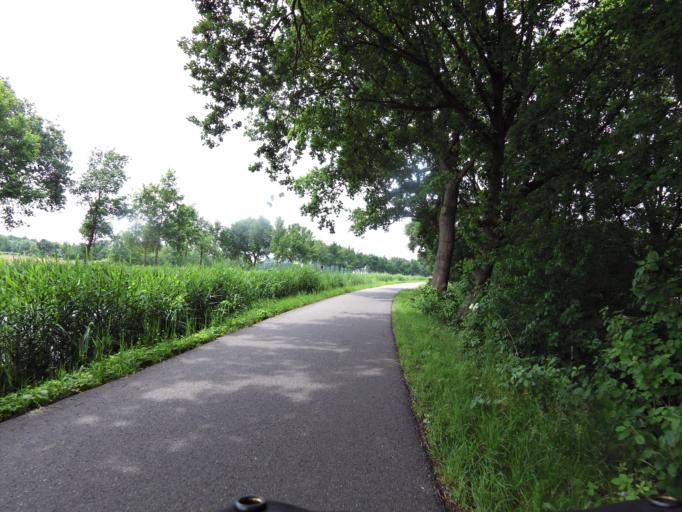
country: NL
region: Gelderland
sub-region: Gemeente Apeldoorn
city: Beekbergen
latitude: 52.1631
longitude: 6.0032
